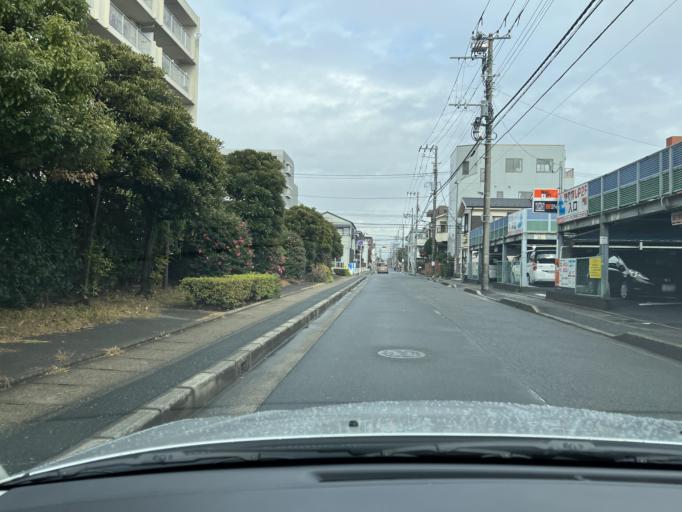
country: JP
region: Tokyo
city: Urayasu
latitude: 35.6872
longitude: 139.9272
